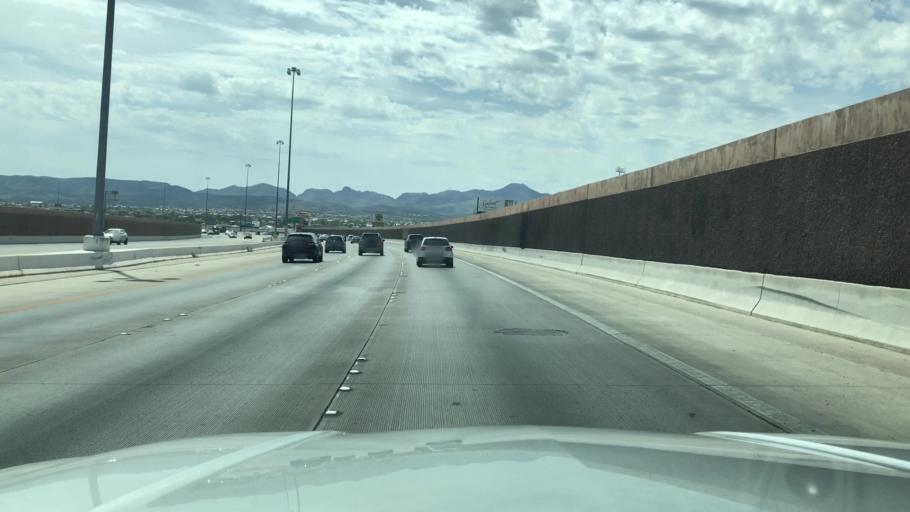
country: US
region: Nevada
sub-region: Clark County
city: Whitney
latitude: 36.0269
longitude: -115.1293
